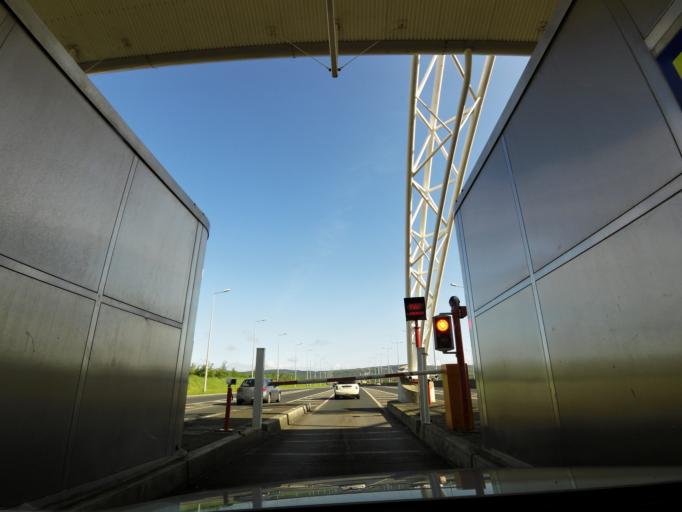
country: IE
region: Munster
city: Moyross
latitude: 52.6696
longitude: -8.7003
